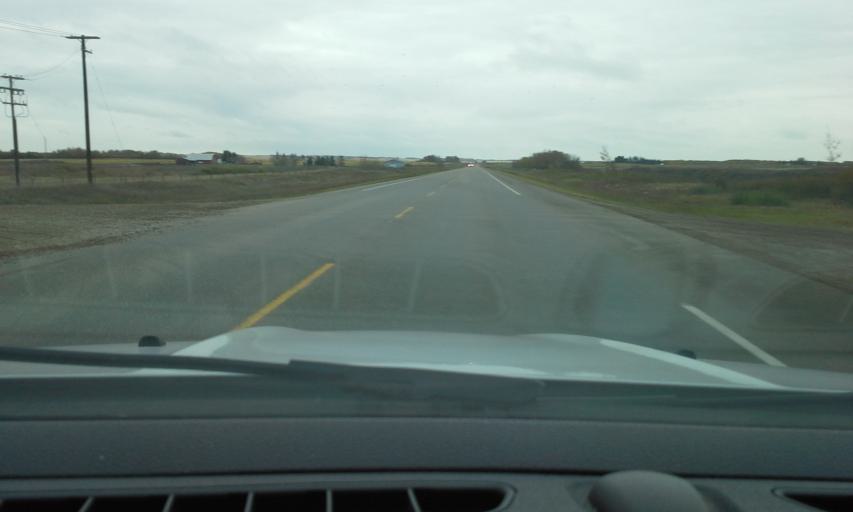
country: CA
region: Saskatchewan
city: Lloydminster
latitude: 53.2779
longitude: -109.8088
